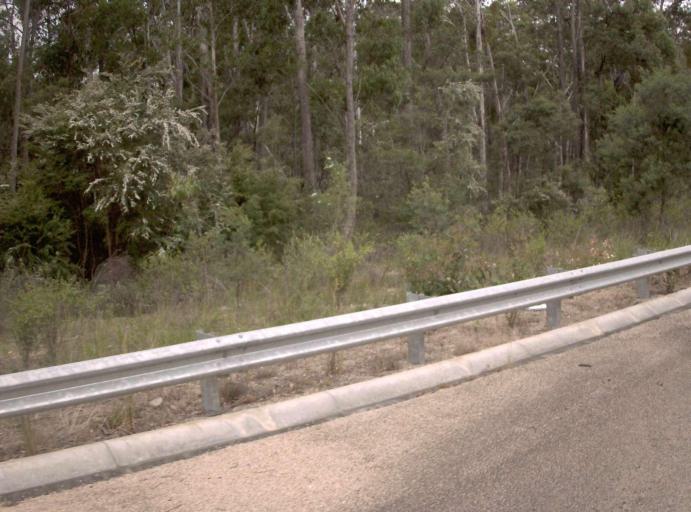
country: AU
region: Victoria
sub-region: East Gippsland
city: Lakes Entrance
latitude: -37.7213
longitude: 148.0821
